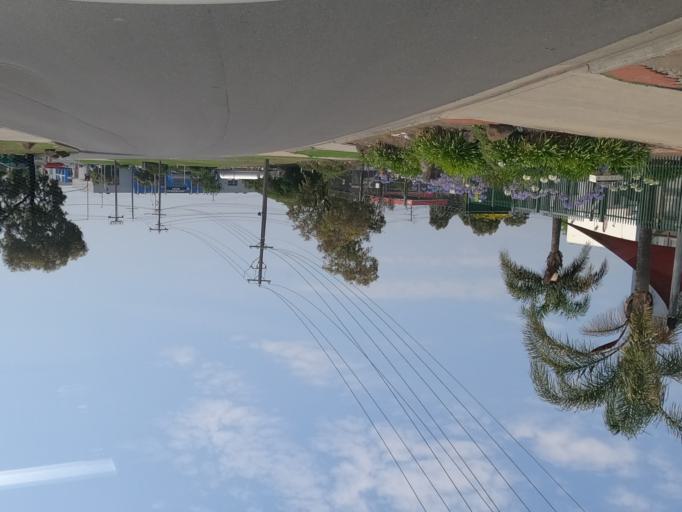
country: AU
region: Victoria
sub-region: Hume
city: Coolaroo
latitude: -37.6443
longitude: 144.9467
